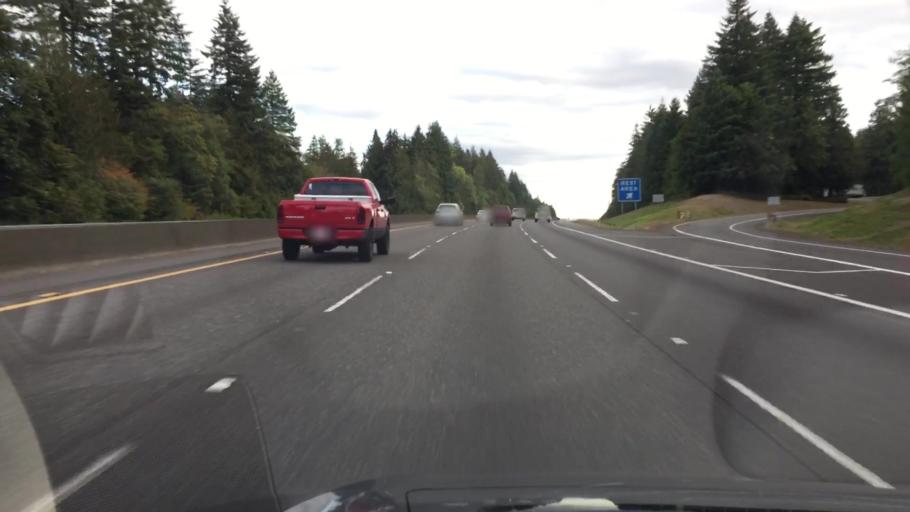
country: US
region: Washington
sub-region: Cowlitz County
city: Castle Rock
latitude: 46.3552
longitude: -122.9060
